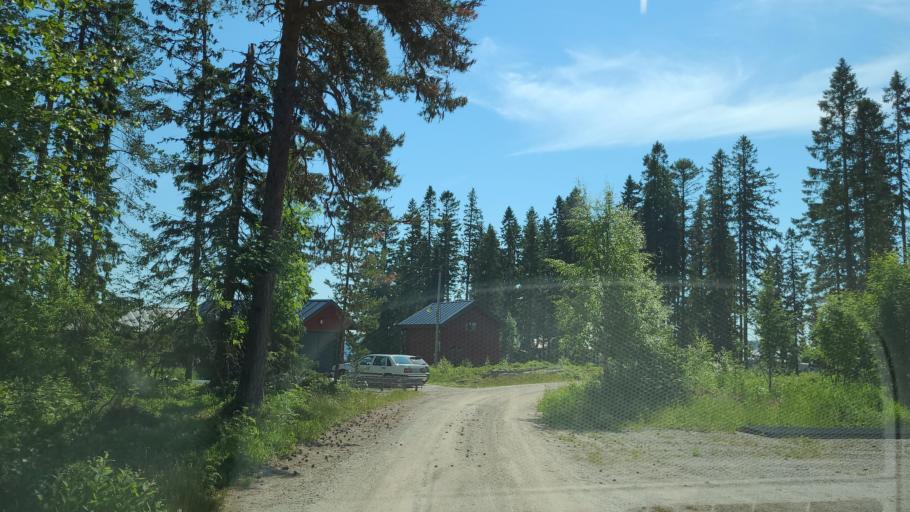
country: SE
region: Vaesterbotten
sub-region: Robertsfors Kommun
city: Robertsfors
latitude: 64.1393
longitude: 20.9630
